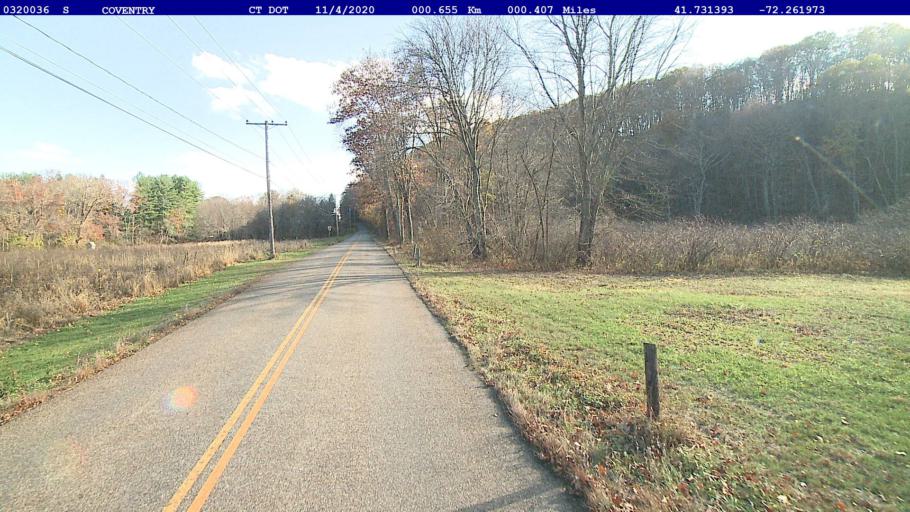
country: US
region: Connecticut
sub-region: Tolland County
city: Mansfield City
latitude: 41.7314
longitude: -72.2620
